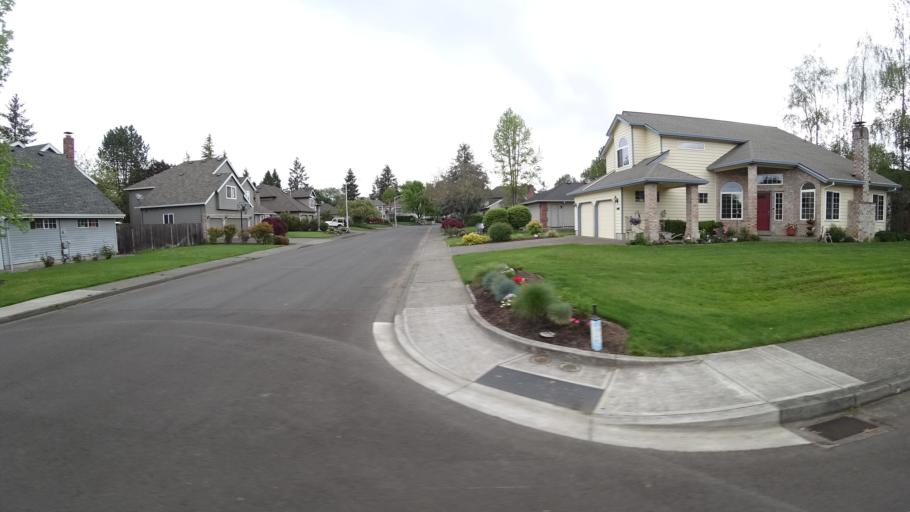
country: US
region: Oregon
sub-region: Washington County
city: Hillsboro
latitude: 45.5380
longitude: -122.9828
